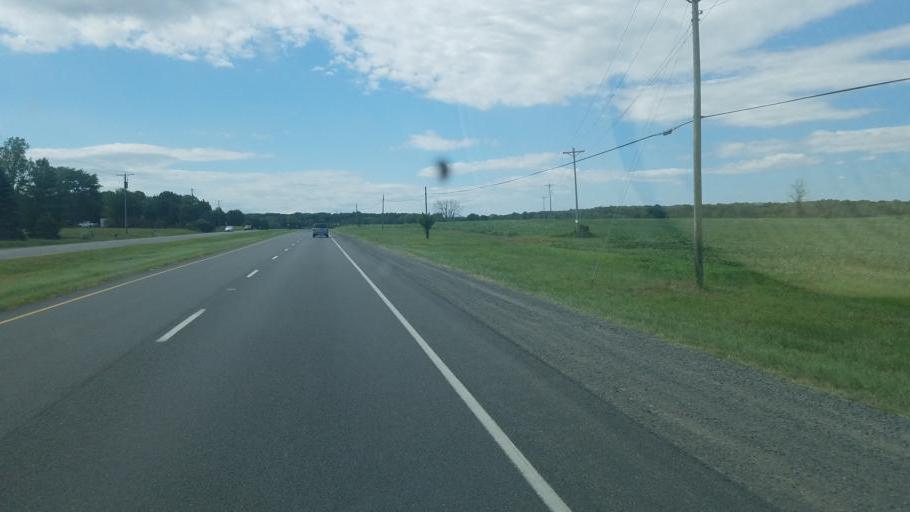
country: US
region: Virginia
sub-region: Fauquier County
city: Bealeton
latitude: 38.5343
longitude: -77.7291
